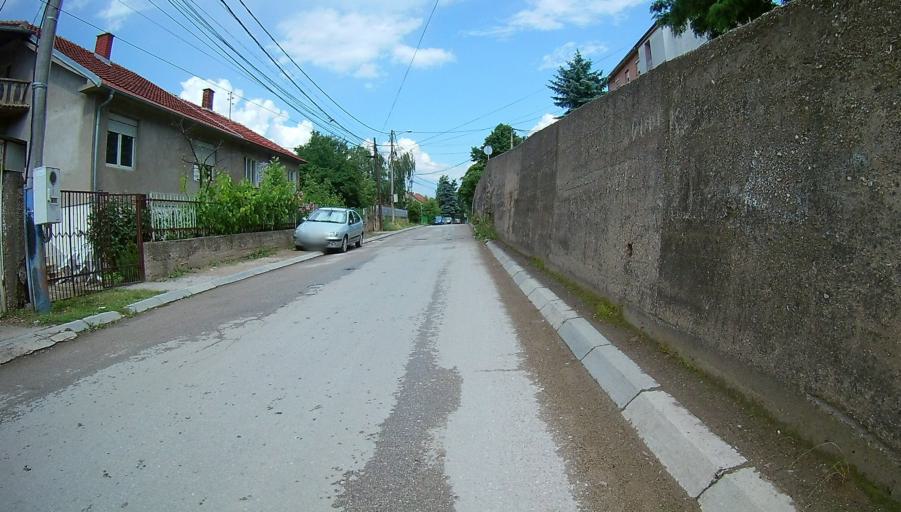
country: RS
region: Central Serbia
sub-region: Nisavski Okrug
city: Nis
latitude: 43.3093
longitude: 21.9017
